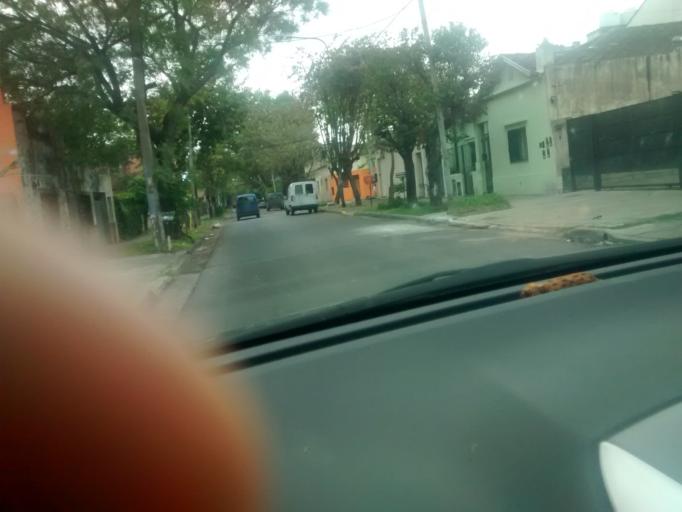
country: AR
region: Buenos Aires
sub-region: Partido de General San Martin
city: General San Martin
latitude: -34.5334
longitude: -58.5172
